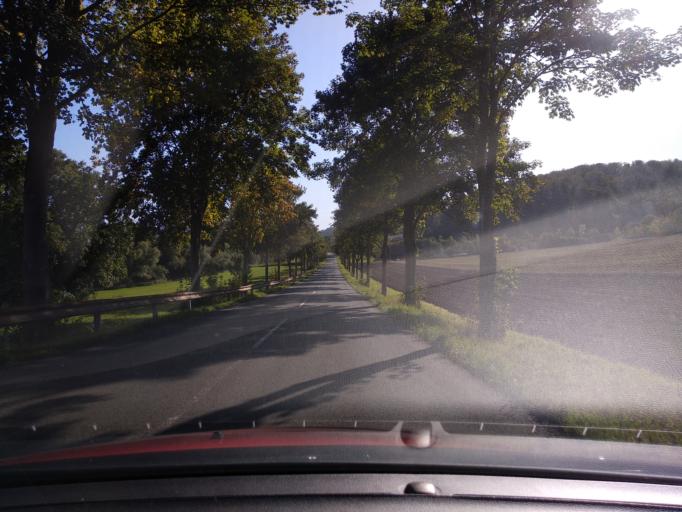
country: DE
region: North Rhine-Westphalia
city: Beverungen
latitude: 51.6910
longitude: 9.3828
